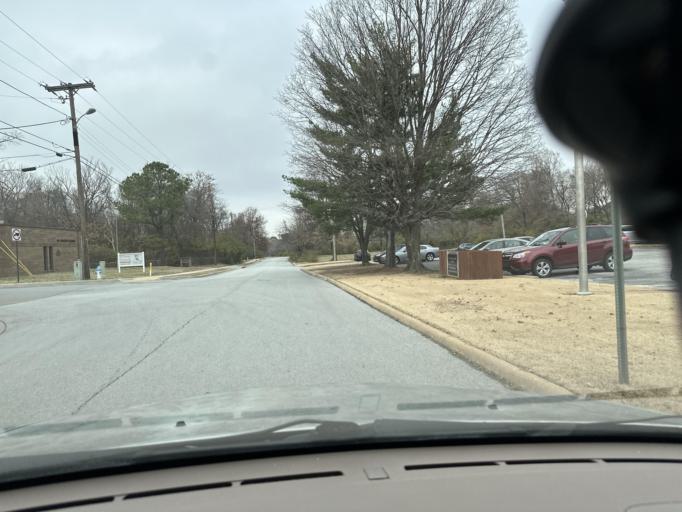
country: US
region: Arkansas
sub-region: Washington County
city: Fayetteville
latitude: 36.0902
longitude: -94.1555
